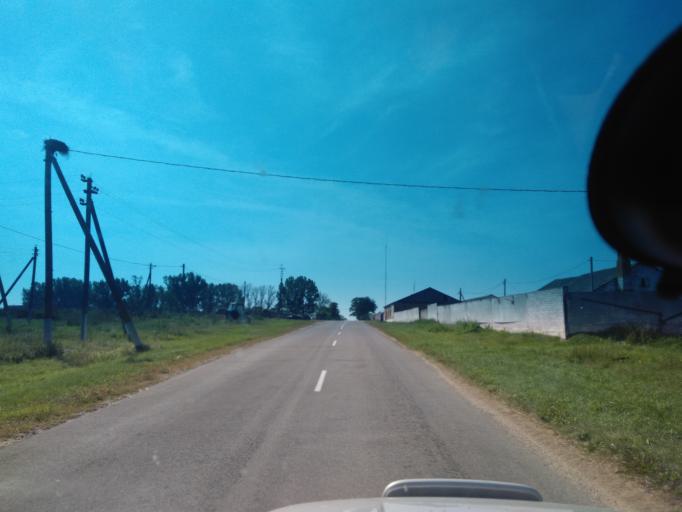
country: BY
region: Minsk
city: Kapyl'
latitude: 53.2106
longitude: 27.1243
